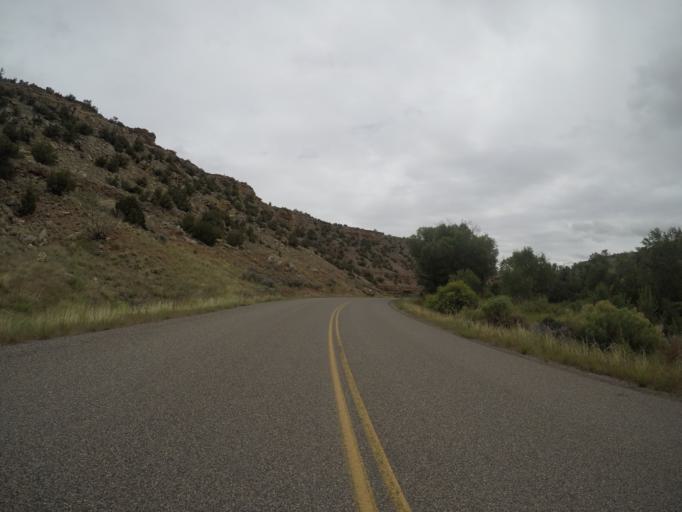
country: US
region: Wyoming
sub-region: Big Horn County
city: Lovell
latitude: 45.1074
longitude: -108.2284
